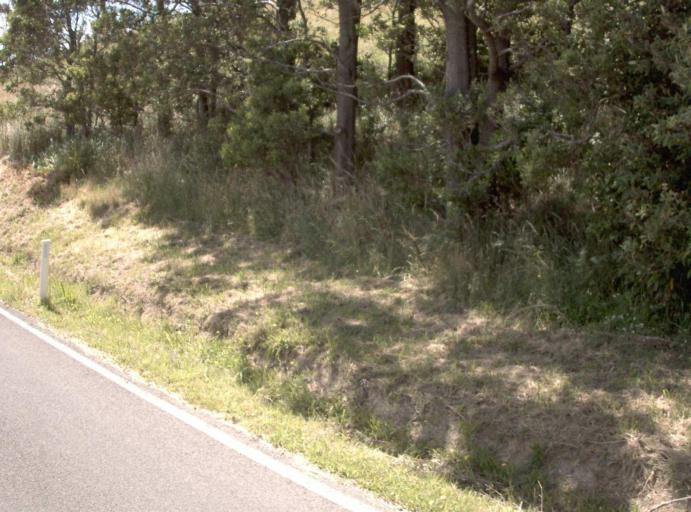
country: AU
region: Victoria
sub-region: Baw Baw
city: Warragul
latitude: -38.3409
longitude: 145.9030
